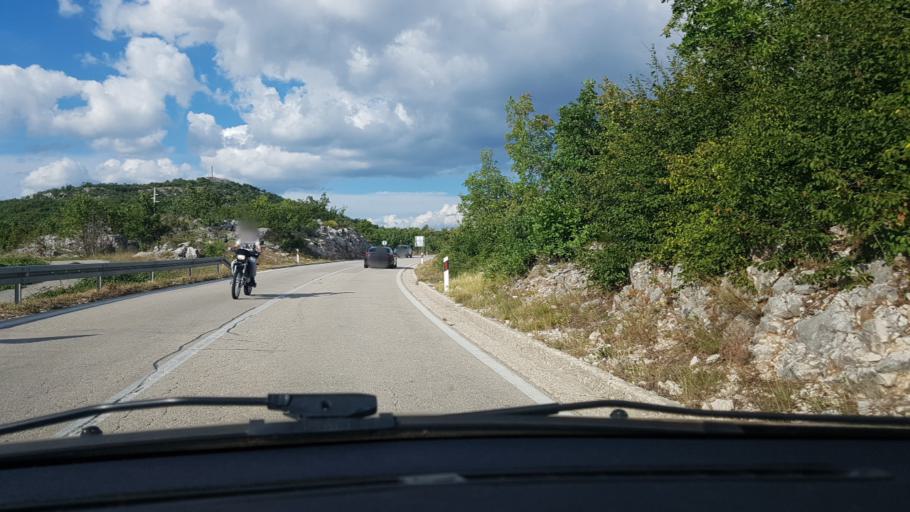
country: HR
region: Splitsko-Dalmatinska
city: Grubine
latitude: 43.4161
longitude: 17.0970
